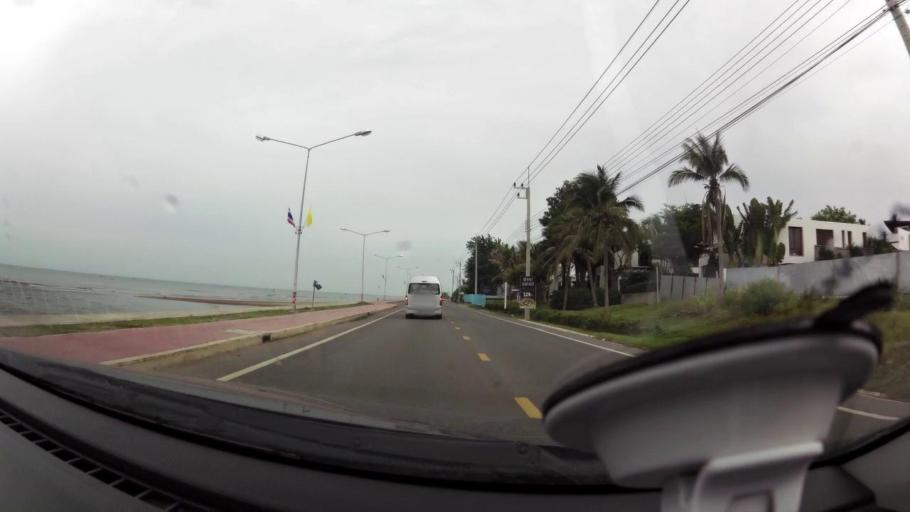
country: TH
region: Prachuap Khiri Khan
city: Pran Buri
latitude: 12.3938
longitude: 99.9963
